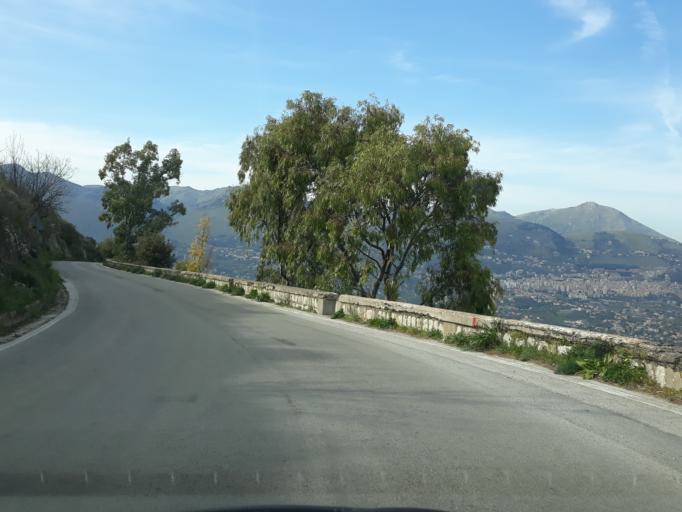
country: IT
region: Sicily
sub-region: Palermo
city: Piano Maglio-Blandino
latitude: 38.0440
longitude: 13.3099
